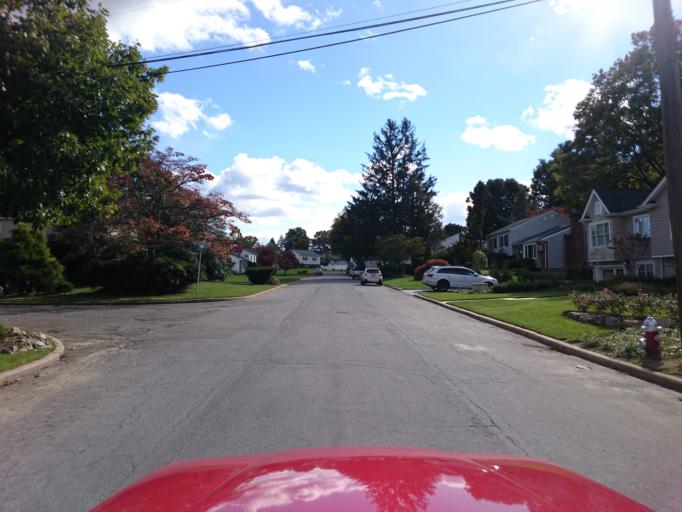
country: US
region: New York
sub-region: Nassau County
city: Glen Cove
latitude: 40.8704
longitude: -73.6451
